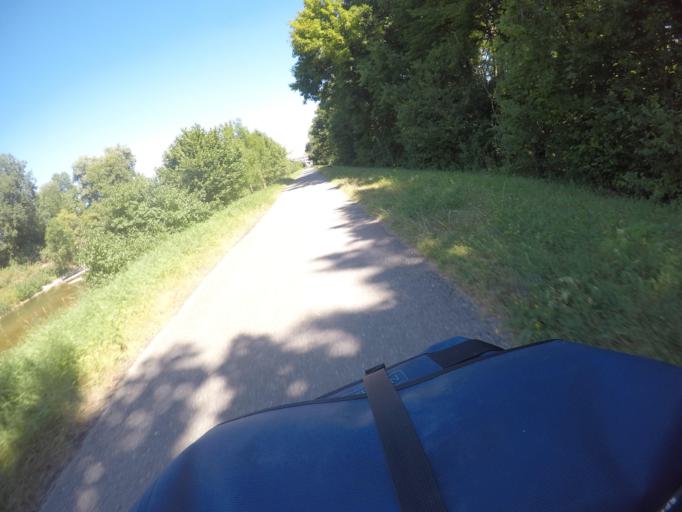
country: DE
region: Baden-Wuerttemberg
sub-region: Tuebingen Region
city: Riedlingen
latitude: 48.1490
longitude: 9.4759
